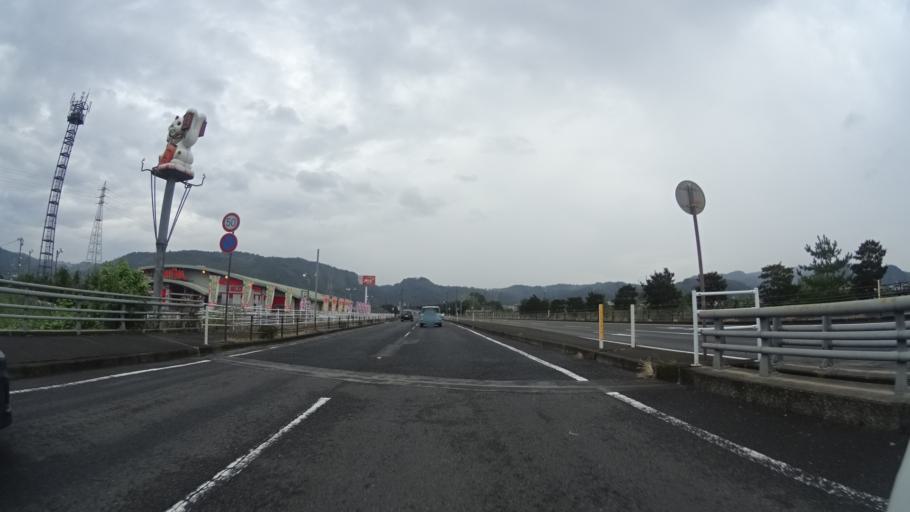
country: JP
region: Kagoshima
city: Kajiki
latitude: 31.7443
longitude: 130.6563
